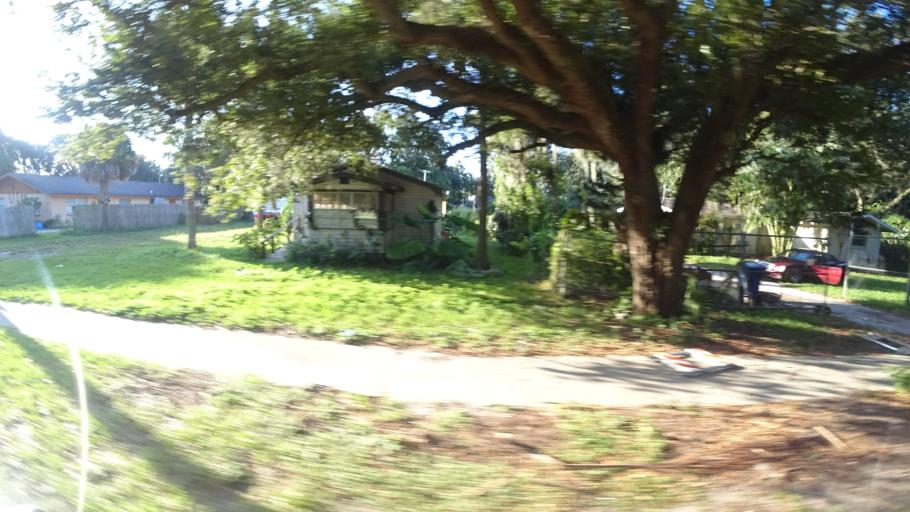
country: US
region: Florida
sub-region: Manatee County
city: Samoset
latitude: 27.4511
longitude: -82.5385
